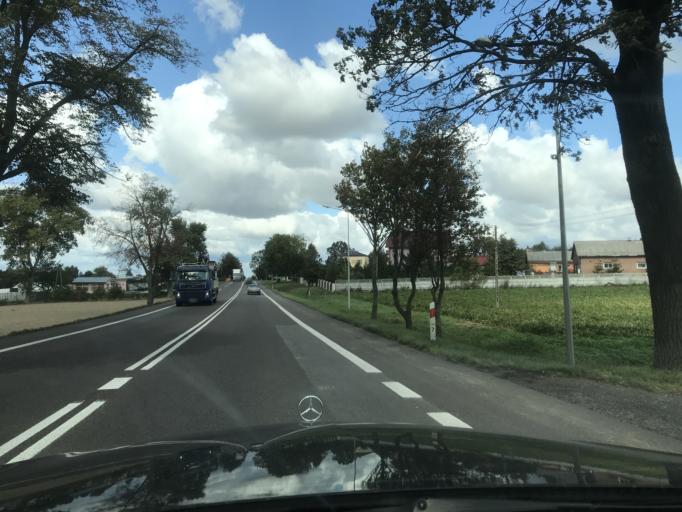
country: PL
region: Lublin Voivodeship
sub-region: Powiat lubelski
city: Niedrzwica Duza
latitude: 51.0606
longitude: 22.3830
